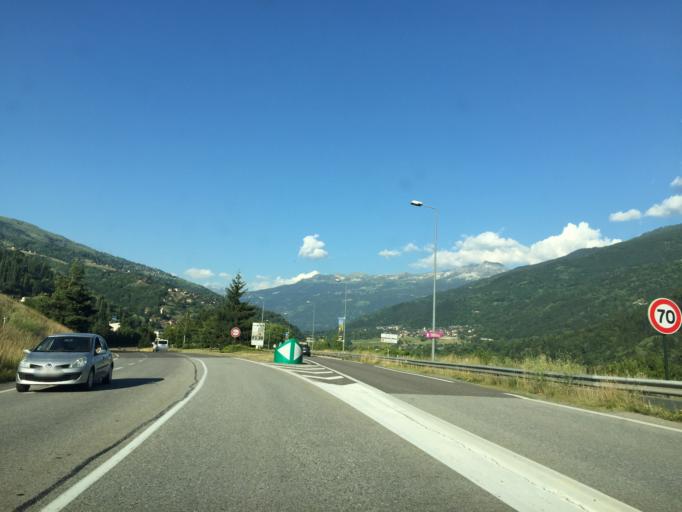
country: FR
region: Rhone-Alpes
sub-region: Departement de la Savoie
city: Aime
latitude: 45.5516
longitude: 6.6341
